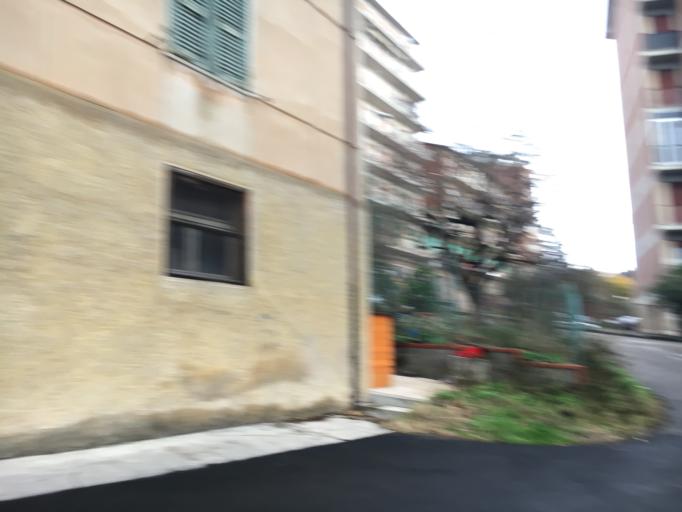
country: IT
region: Umbria
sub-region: Provincia di Perugia
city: Perugia
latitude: 43.1164
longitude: 12.3768
